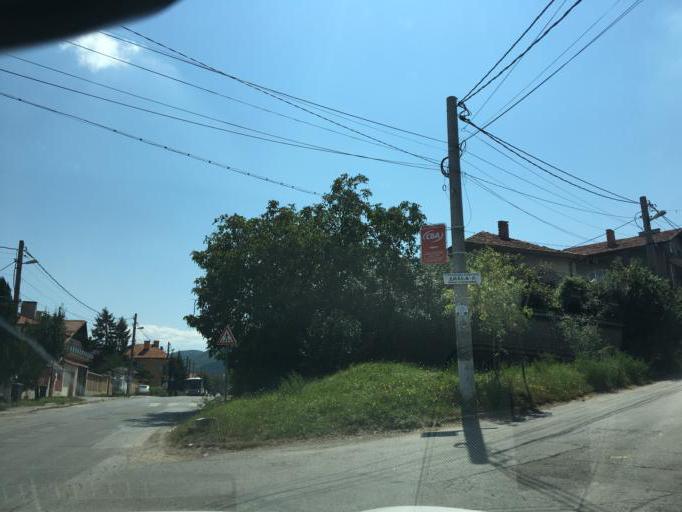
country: BG
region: Sofiya
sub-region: Obshtina Elin Pelin
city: Elin Pelin
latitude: 42.6068
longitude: 23.4692
